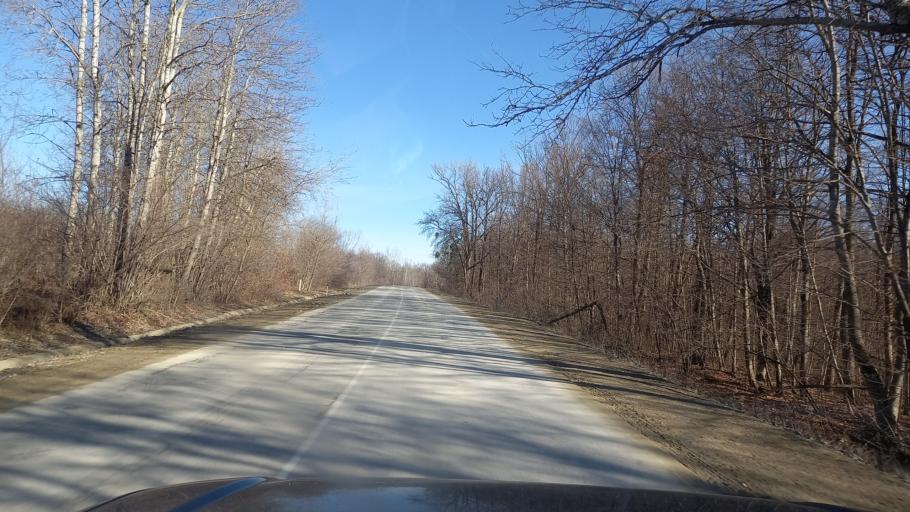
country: RU
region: Adygeya
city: Kamennomostskiy
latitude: 44.2796
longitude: 40.2445
